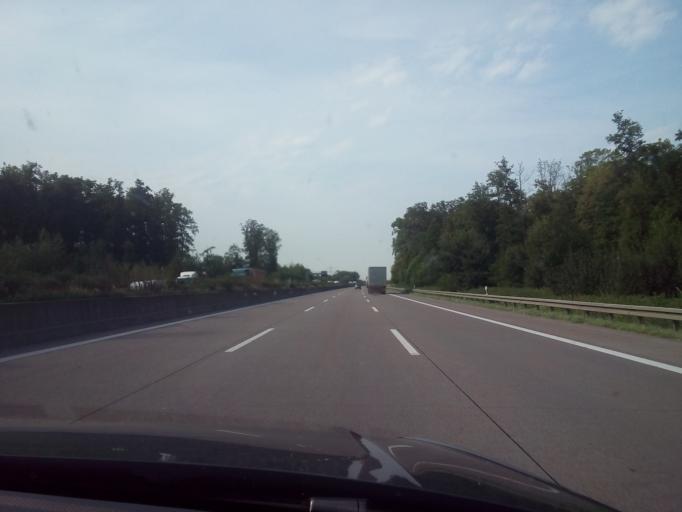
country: DE
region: Baden-Wuerttemberg
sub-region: Freiburg Region
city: Renchen
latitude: 48.6341
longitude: 8.0236
